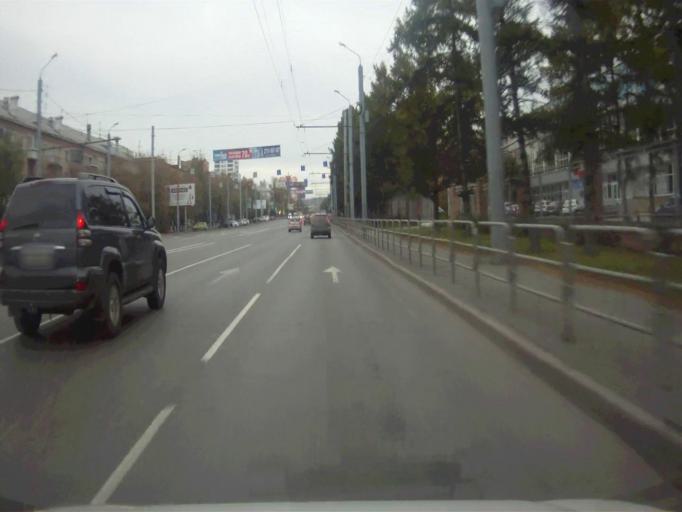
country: RU
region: Chelyabinsk
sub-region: Gorod Chelyabinsk
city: Chelyabinsk
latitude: 55.1653
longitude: 61.3806
